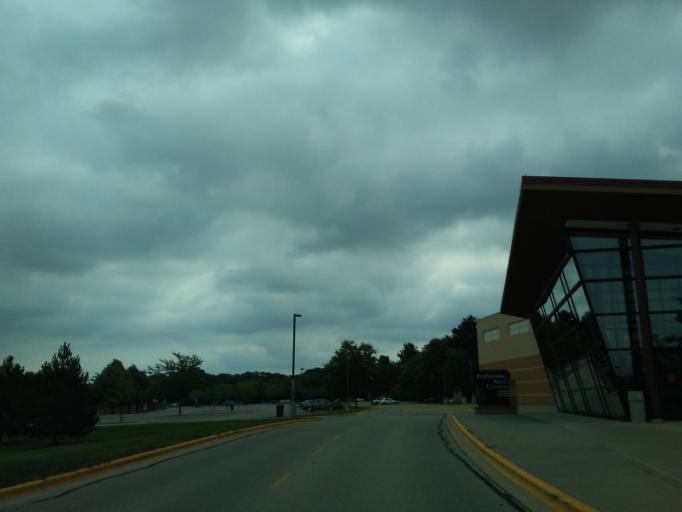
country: US
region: Wisconsin
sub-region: Dane County
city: Middleton
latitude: 43.1013
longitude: -89.5083
